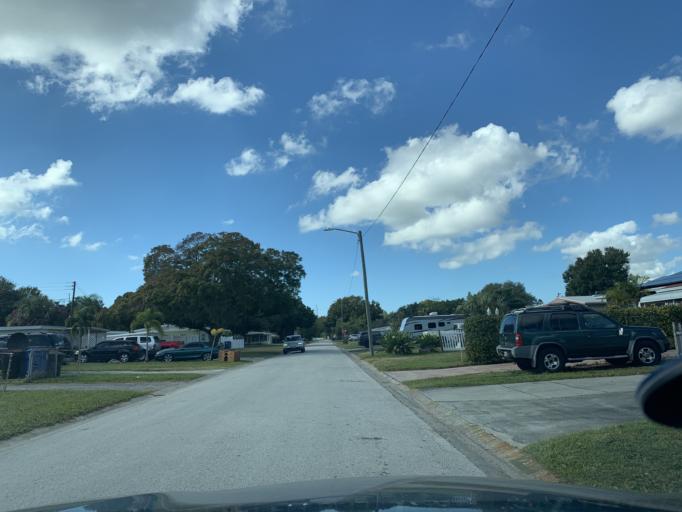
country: US
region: Florida
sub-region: Pinellas County
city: Kenneth City
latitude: 27.8046
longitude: -82.7399
